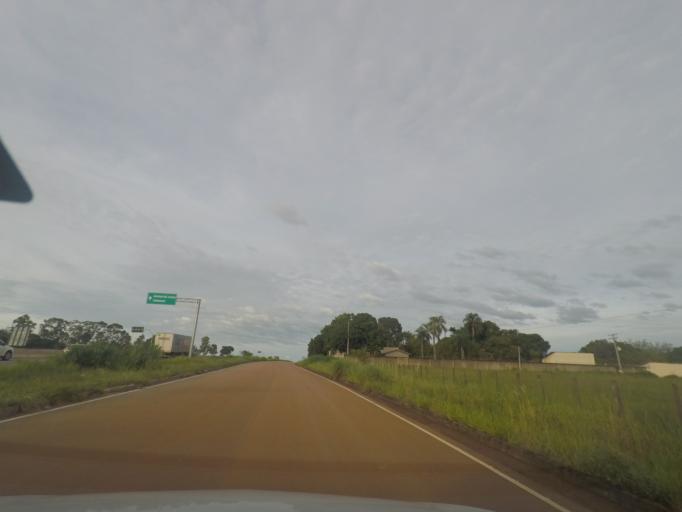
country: BR
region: Goias
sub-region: Trindade
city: Trindade
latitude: -16.7388
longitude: -49.4094
